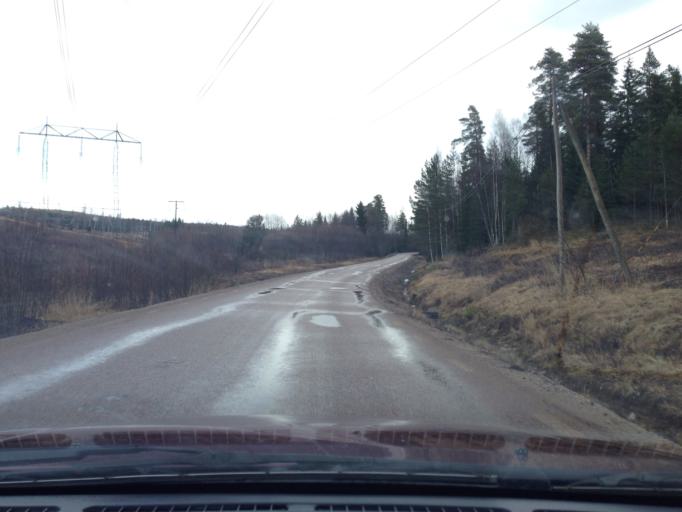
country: SE
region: Dalarna
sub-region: Ludvika Kommun
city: Ludvika
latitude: 60.1722
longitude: 15.2607
